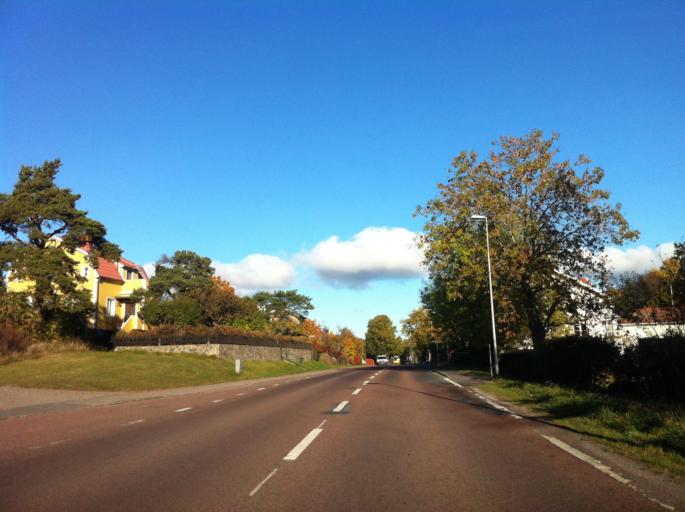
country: SE
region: Uppsala
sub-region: Osthammars Kommun
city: Oregrund
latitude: 60.3342
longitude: 18.4324
